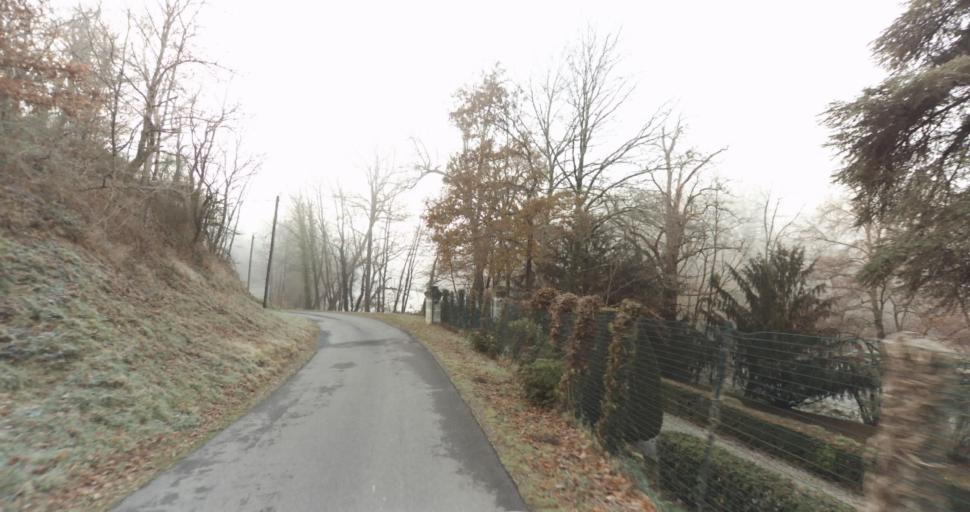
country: FR
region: Limousin
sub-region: Departement de la Haute-Vienne
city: Saint-Priest-sous-Aixe
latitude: 45.8181
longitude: 1.1195
